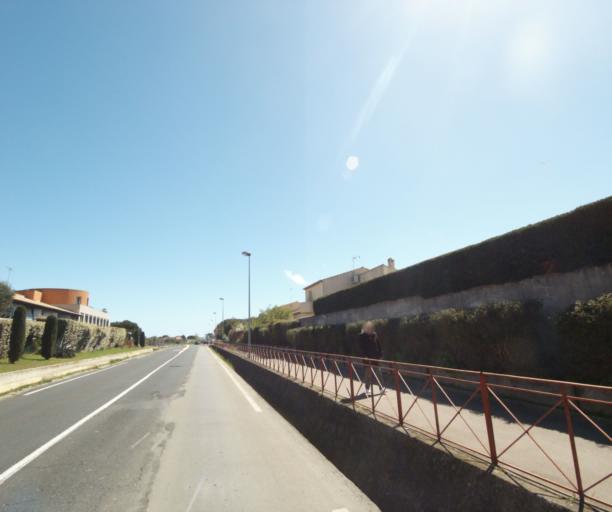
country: FR
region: Languedoc-Roussillon
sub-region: Departement de l'Herault
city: Perols
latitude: 43.5580
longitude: 3.9620
